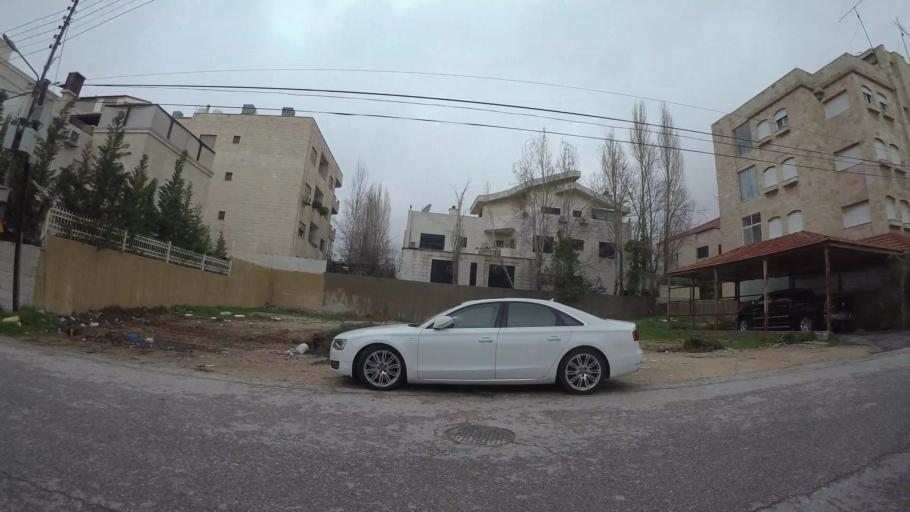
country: JO
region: Amman
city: Wadi as Sir
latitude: 31.9450
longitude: 35.8615
